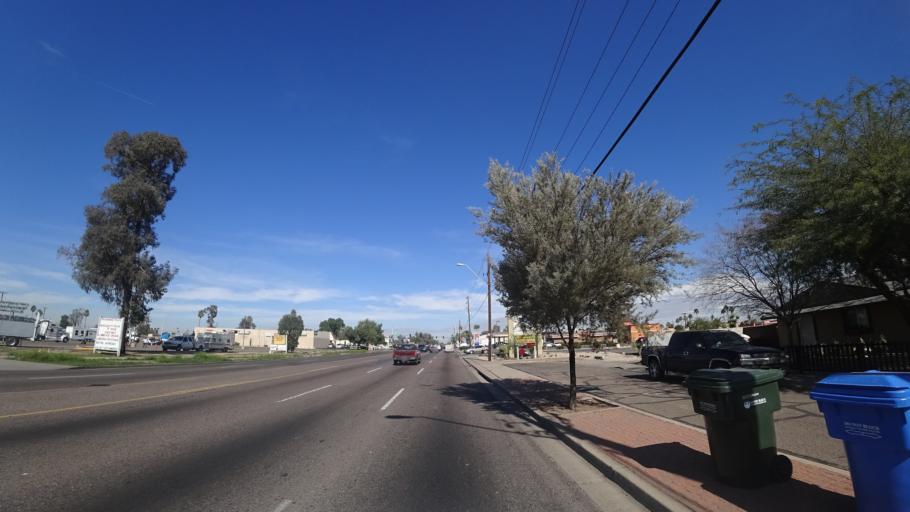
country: US
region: Arizona
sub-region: Maricopa County
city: Glendale
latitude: 33.4787
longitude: -112.2032
